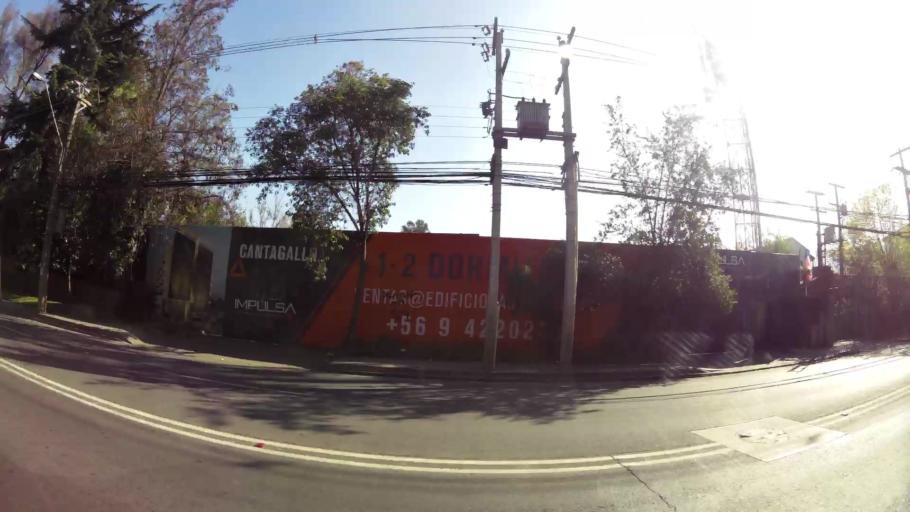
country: CL
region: Santiago Metropolitan
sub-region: Provincia de Santiago
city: Villa Presidente Frei, Nunoa, Santiago, Chile
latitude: -33.3738
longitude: -70.5170
